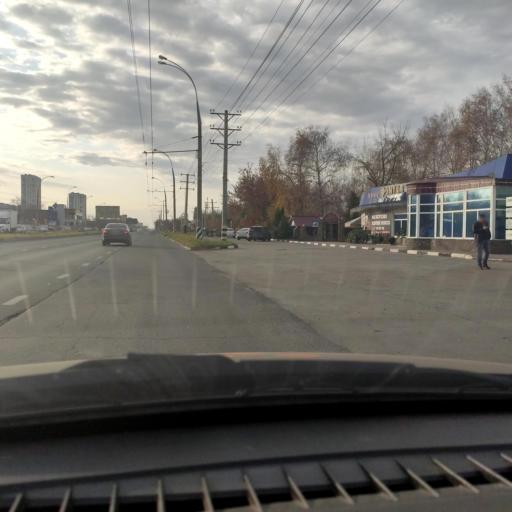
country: RU
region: Samara
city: Tol'yatti
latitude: 53.5493
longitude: 49.3022
